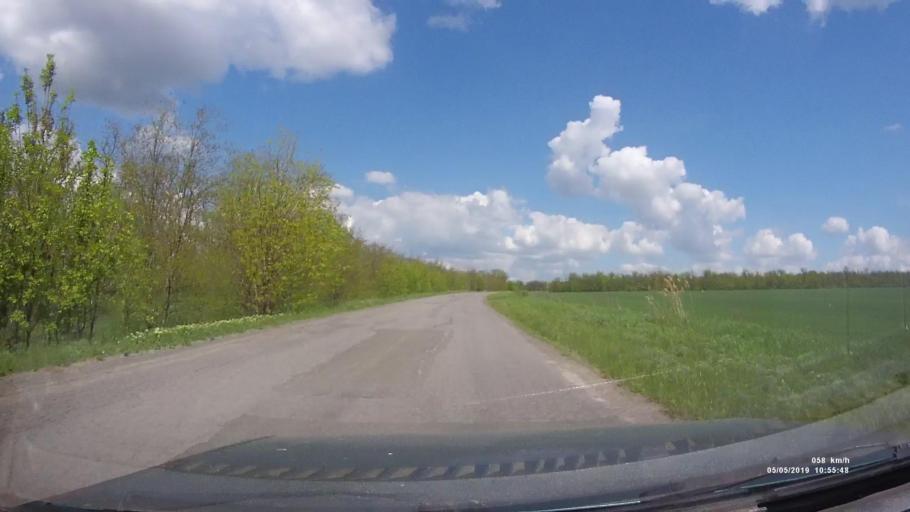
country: RU
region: Rostov
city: Ust'-Donetskiy
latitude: 47.6688
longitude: 40.8203
